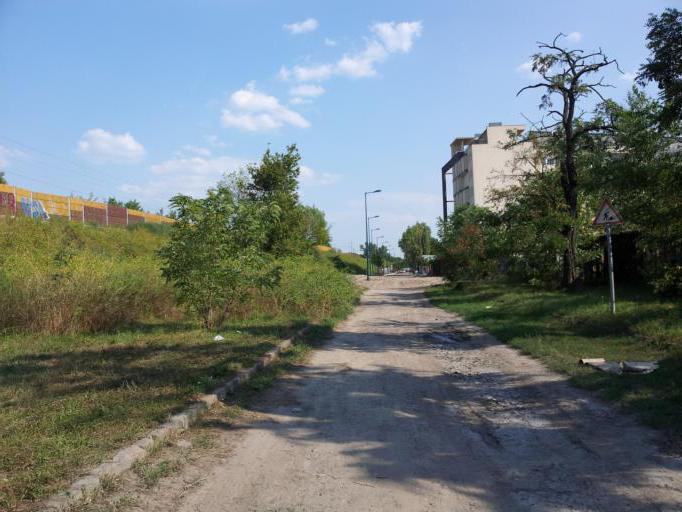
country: HU
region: Budapest
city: Budapest XIV. keruelet
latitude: 47.5056
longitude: 19.1091
